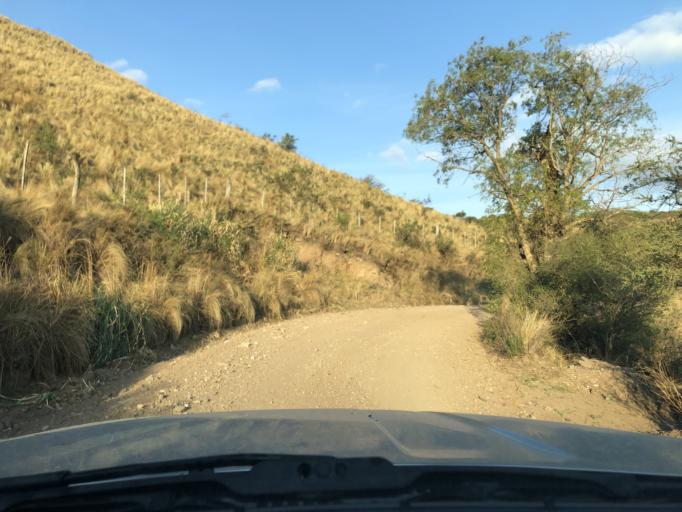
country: AR
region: Cordoba
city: Agua de Oro
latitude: -31.0555
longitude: -64.3532
